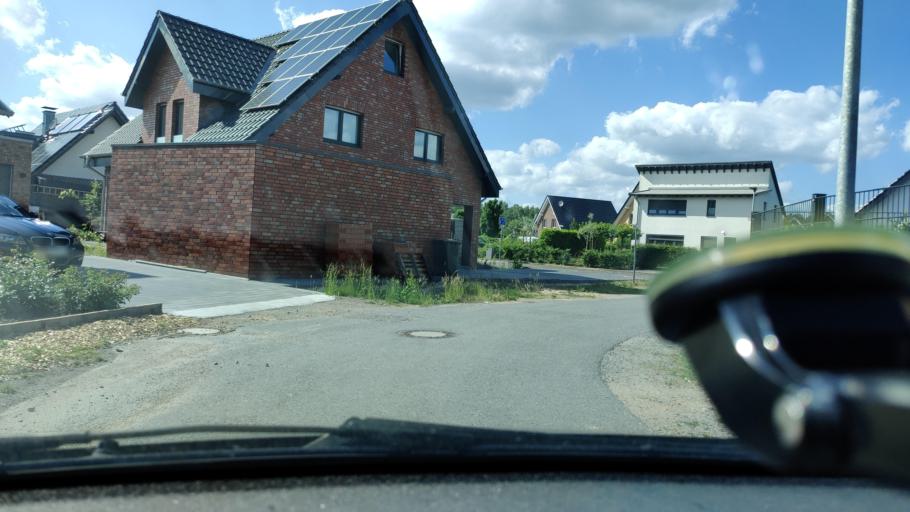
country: DE
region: North Rhine-Westphalia
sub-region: Regierungsbezirk Munster
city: Velen
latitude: 51.8880
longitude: 6.9301
